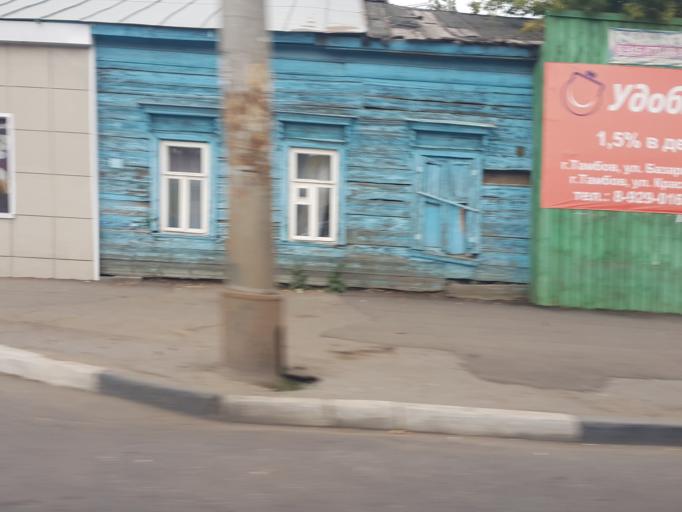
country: RU
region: Tambov
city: Tambov
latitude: 52.7248
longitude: 41.4408
